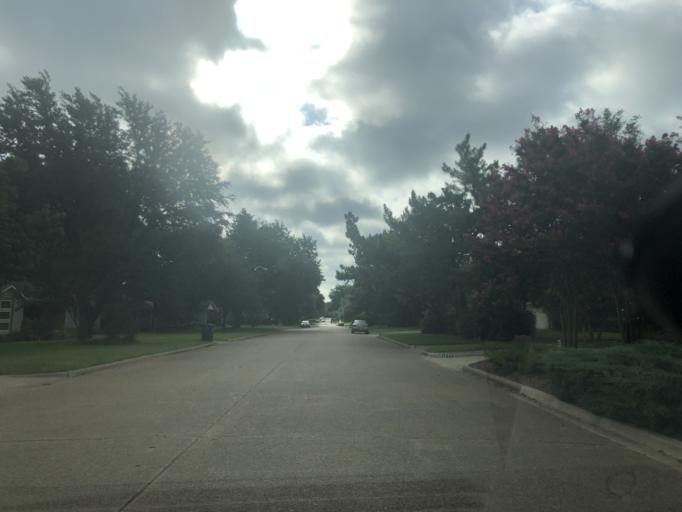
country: US
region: Texas
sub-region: Dallas County
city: University Park
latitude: 32.8710
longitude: -96.8443
